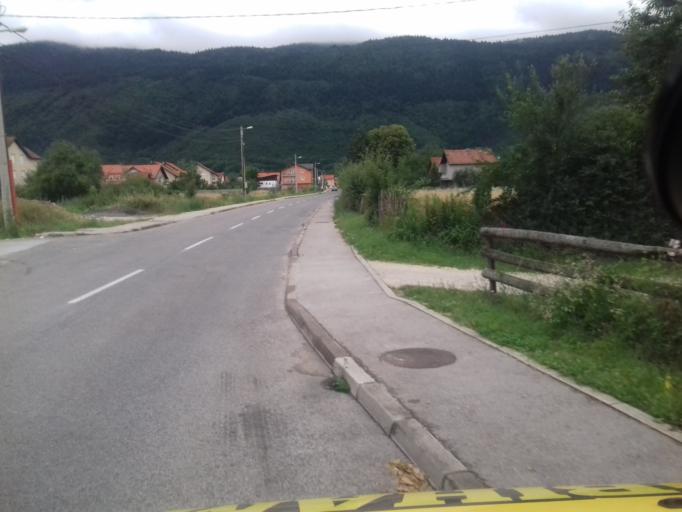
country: BA
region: Federation of Bosnia and Herzegovina
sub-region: Kanton Sarajevo
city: Sarajevo
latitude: 43.8132
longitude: 18.3053
